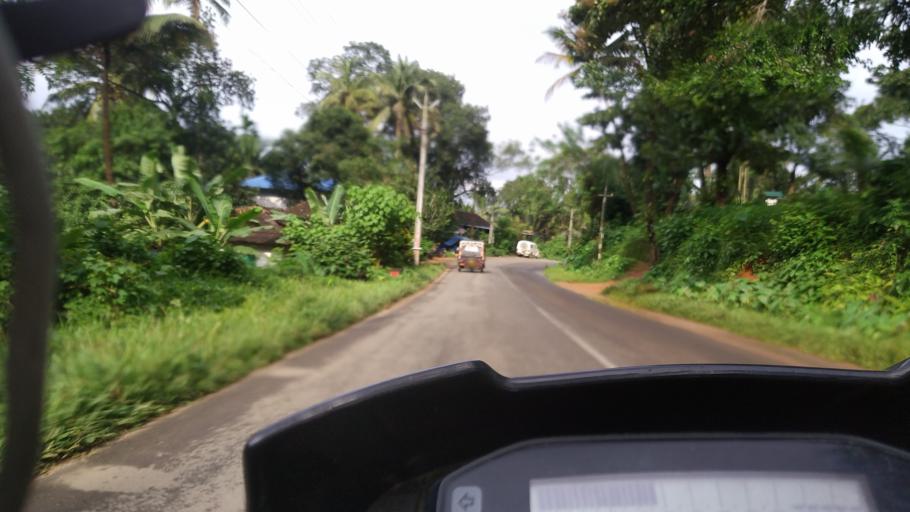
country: IN
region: Kerala
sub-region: Ernakulam
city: Kotamangalam
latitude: 10.0513
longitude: 76.7106
